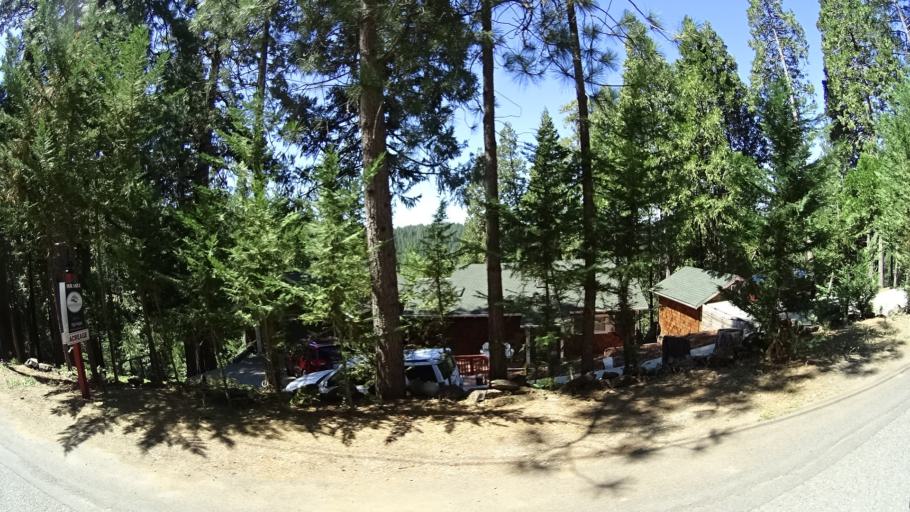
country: US
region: California
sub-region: Calaveras County
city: Arnold
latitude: 38.2400
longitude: -120.3369
